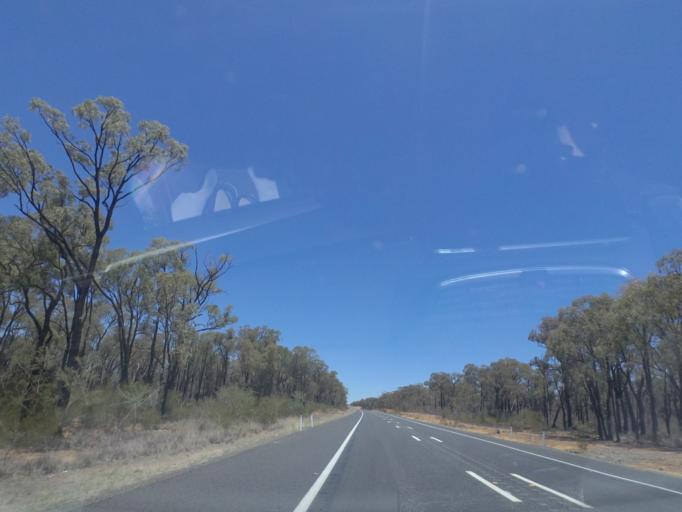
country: AU
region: New South Wales
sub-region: Warrumbungle Shire
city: Coonabarabran
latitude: -30.8879
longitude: 149.4435
